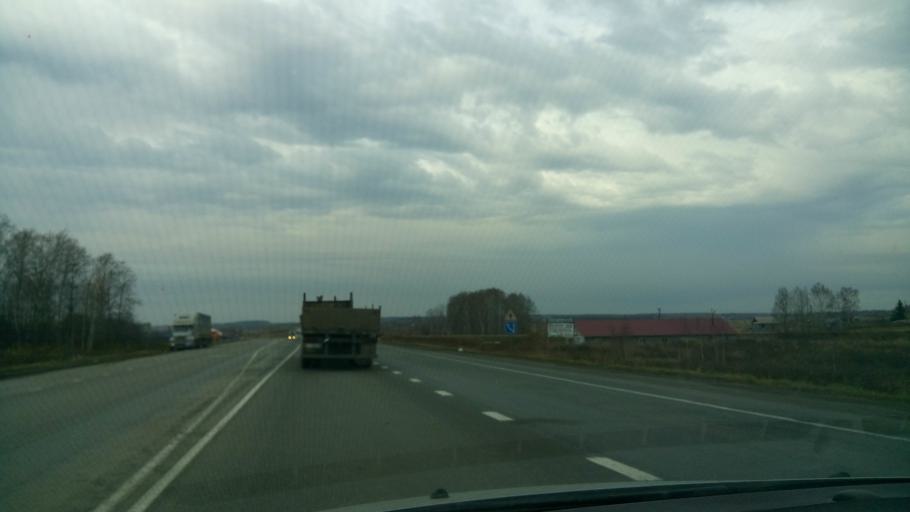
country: RU
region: Sverdlovsk
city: Kamyshlov
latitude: 56.8697
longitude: 62.7457
